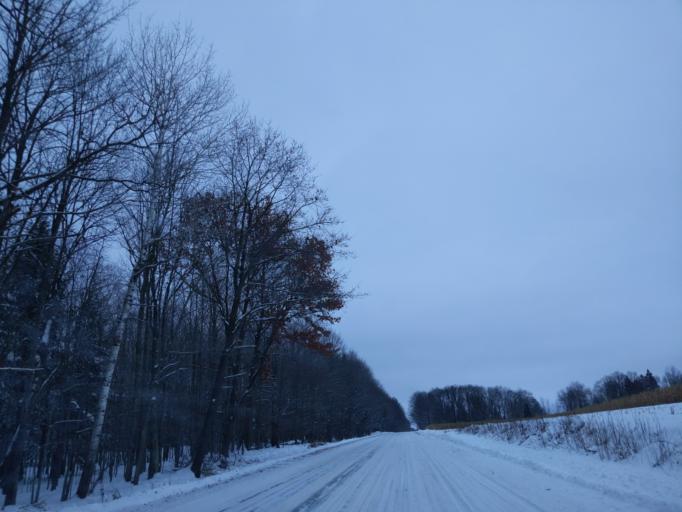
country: US
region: Wisconsin
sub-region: Marathon County
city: Mosinee
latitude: 44.7718
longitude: -89.8598
